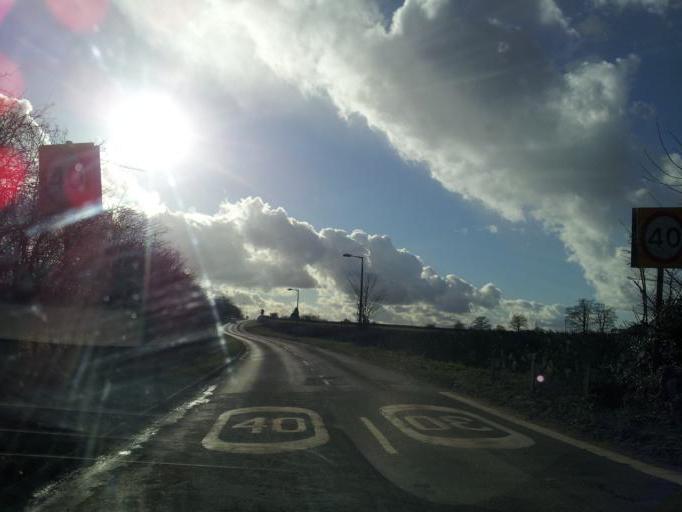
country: GB
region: England
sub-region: Derbyshire
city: Blackwell
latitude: 53.1194
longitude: -1.3603
